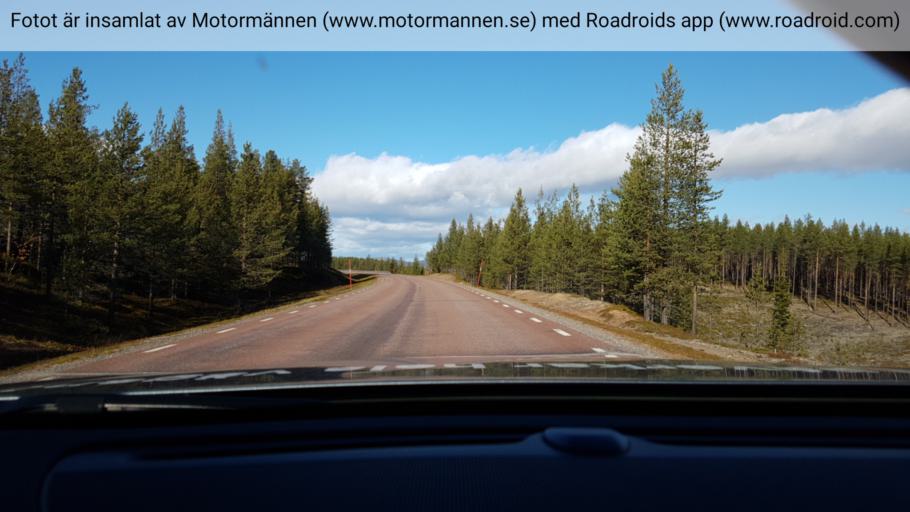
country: SE
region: Norrbotten
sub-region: Arjeplogs Kommun
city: Arjeplog
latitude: 66.0326
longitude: 18.0574
